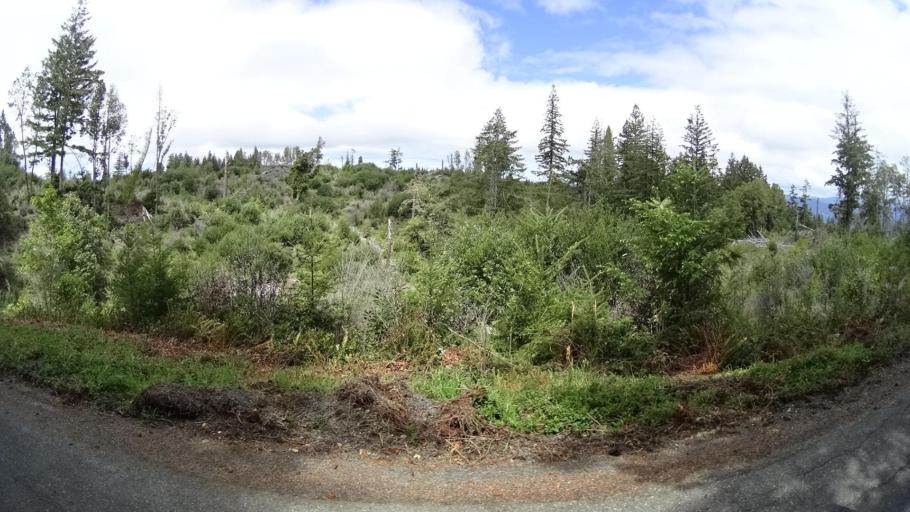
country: US
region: California
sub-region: Humboldt County
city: Blue Lake
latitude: 40.7938
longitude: -123.9726
